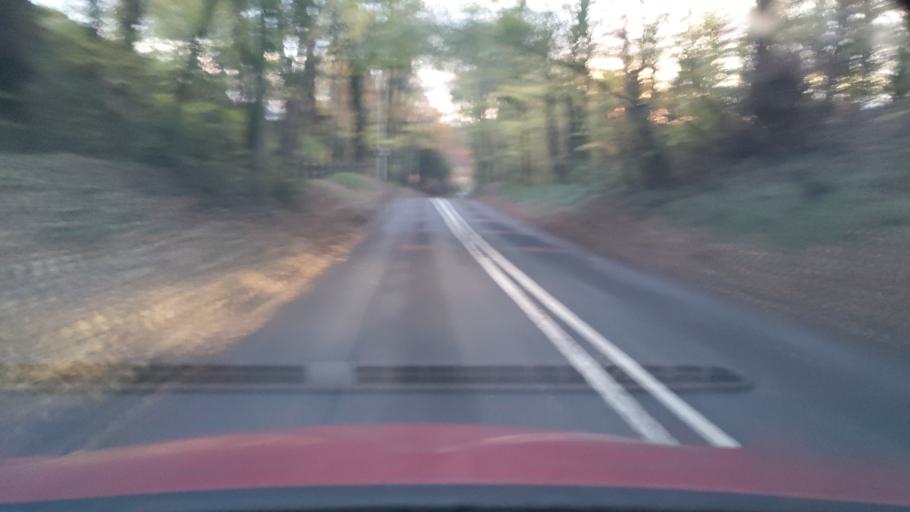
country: GB
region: England
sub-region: Lancashire
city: Clayton-le-Woods
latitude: 53.7024
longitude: -2.6502
